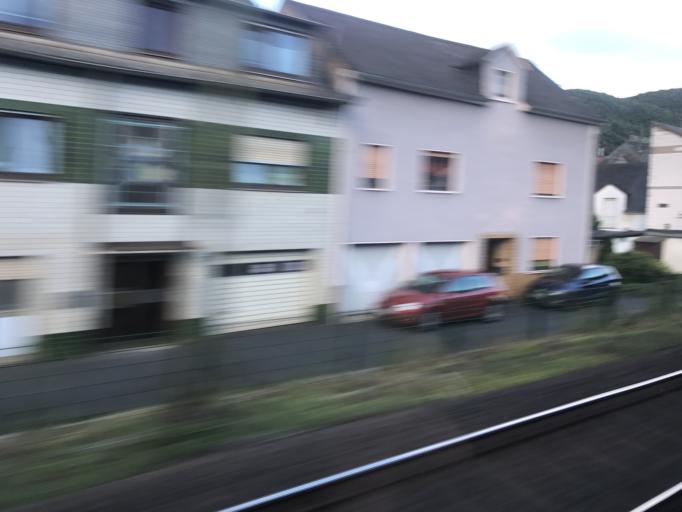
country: DE
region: Rheinland-Pfalz
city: Kamp-Bornhofen
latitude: 50.2072
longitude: 7.6328
